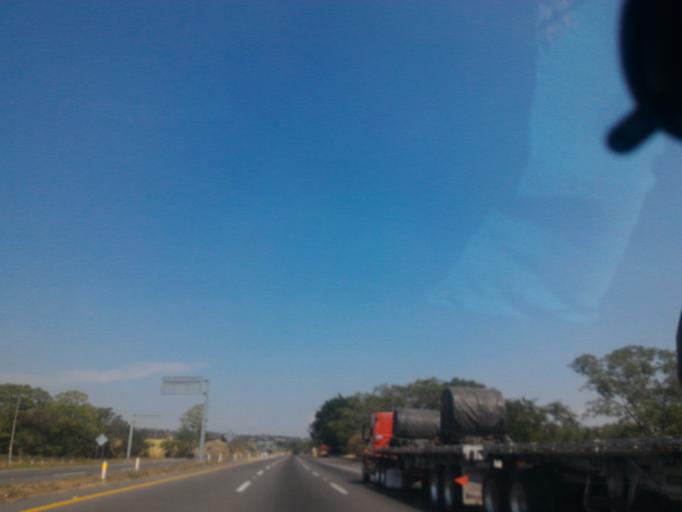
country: MX
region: Colima
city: Cuauhtemoc
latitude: 19.3131
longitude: -103.6011
